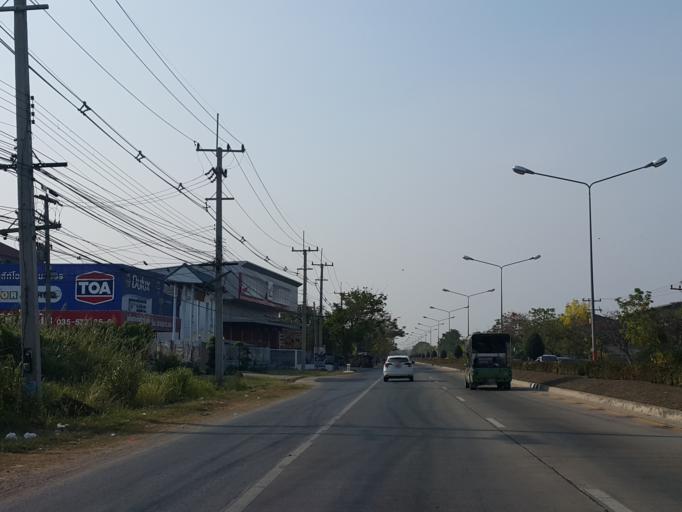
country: TH
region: Suphan Buri
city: Sam Chuk
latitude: 14.7581
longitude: 100.0958
